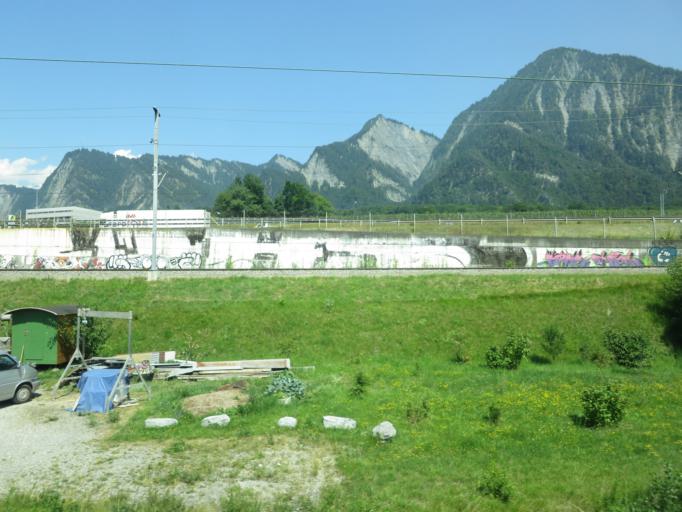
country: CH
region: Grisons
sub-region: Landquart District
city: Zizers
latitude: 46.9265
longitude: 9.5613
